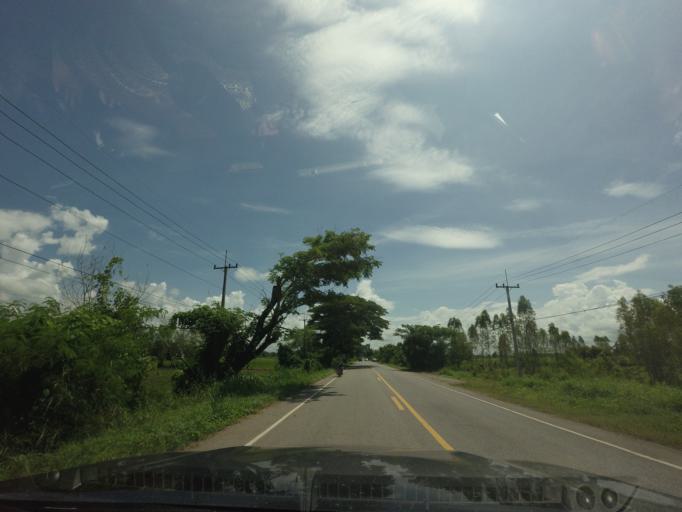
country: TH
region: Changwat Udon Thani
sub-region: Amphoe Ban Phue
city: Ban Phue
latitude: 17.7174
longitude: 102.4042
